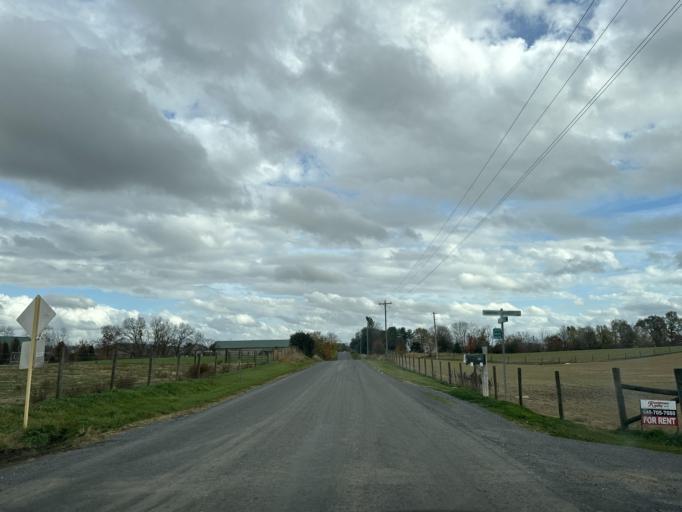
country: US
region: Virginia
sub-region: Rockingham County
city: Dayton
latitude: 38.4135
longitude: -78.9662
